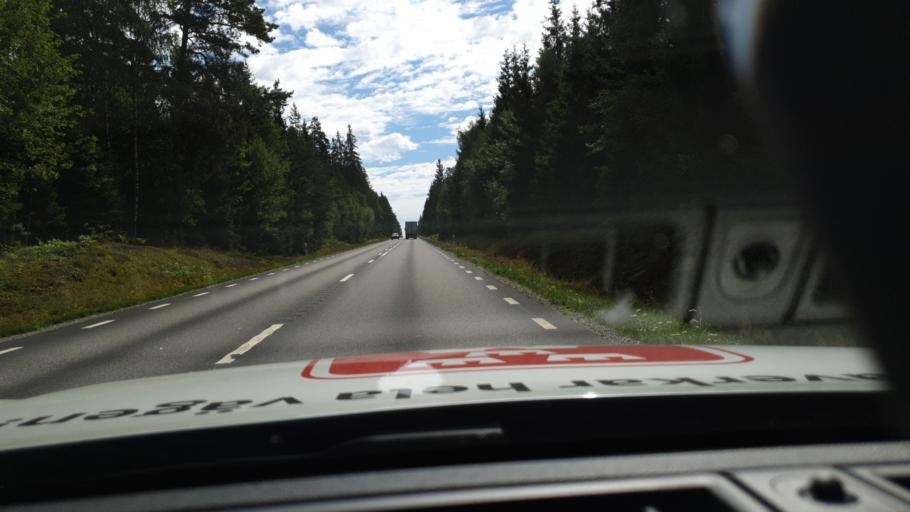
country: SE
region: Joenkoeping
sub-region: Savsjo Kommun
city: Vrigstad
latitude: 57.3276
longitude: 14.4747
